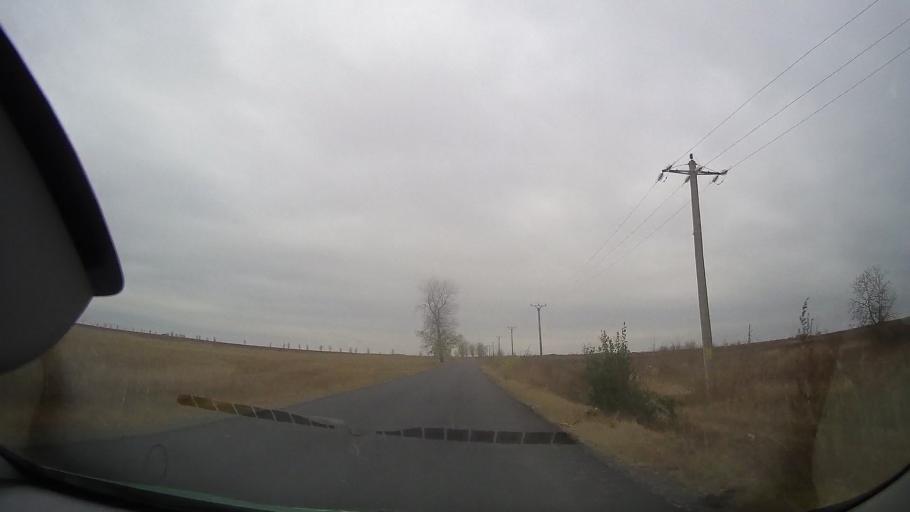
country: RO
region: Braila
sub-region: Comuna Ciresu
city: Ciresu
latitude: 44.9406
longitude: 27.3549
